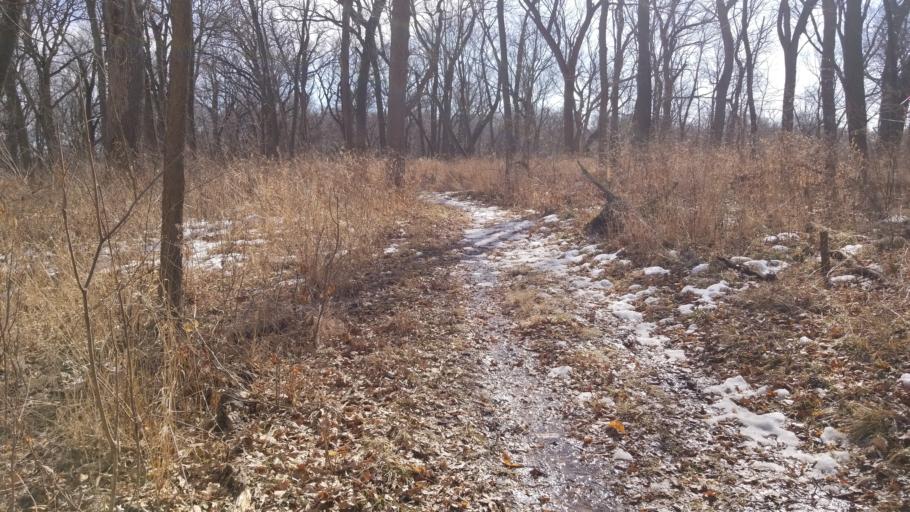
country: US
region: Nebraska
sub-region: Sarpy County
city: Bellevue
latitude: 41.1744
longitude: -95.9019
